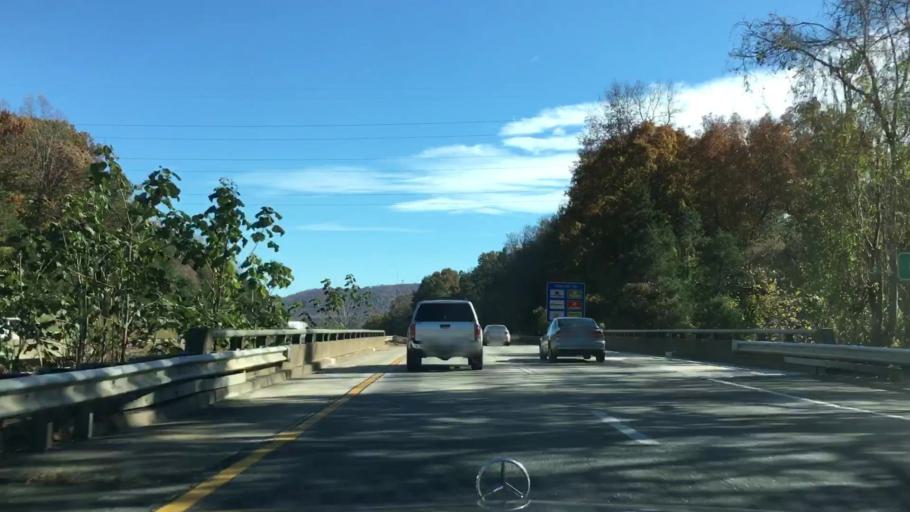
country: US
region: Virginia
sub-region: City of Charlottesville
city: Charlottesville
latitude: 38.0131
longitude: -78.5267
